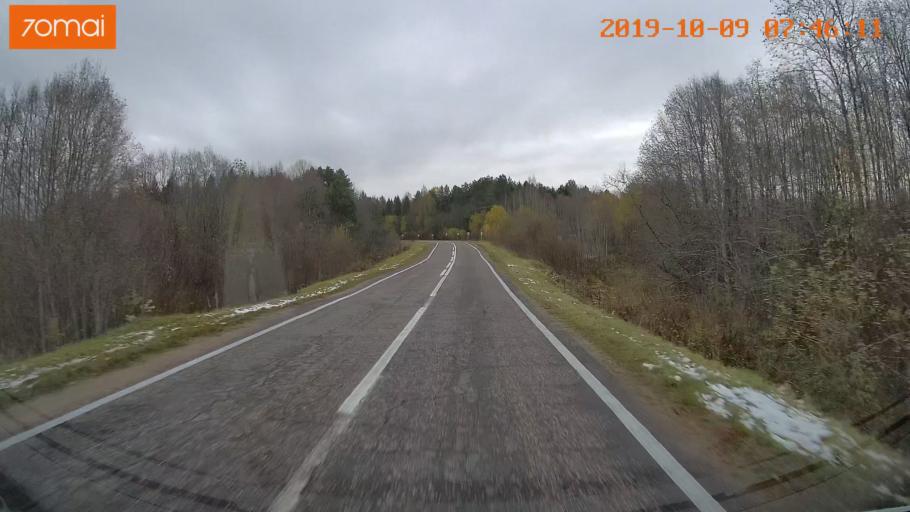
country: RU
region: Jaroslavl
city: Kukoboy
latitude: 58.6557
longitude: 39.7826
